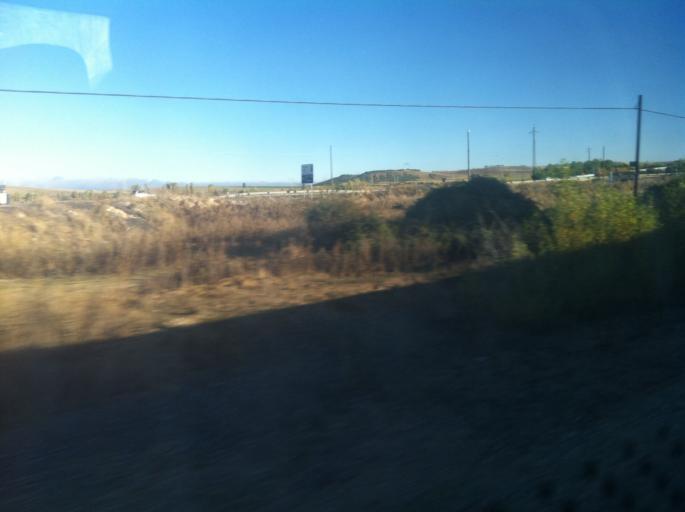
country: ES
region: Castille and Leon
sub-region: Provincia de Palencia
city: Reinoso de Cerrato
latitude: 41.9860
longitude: -4.4165
